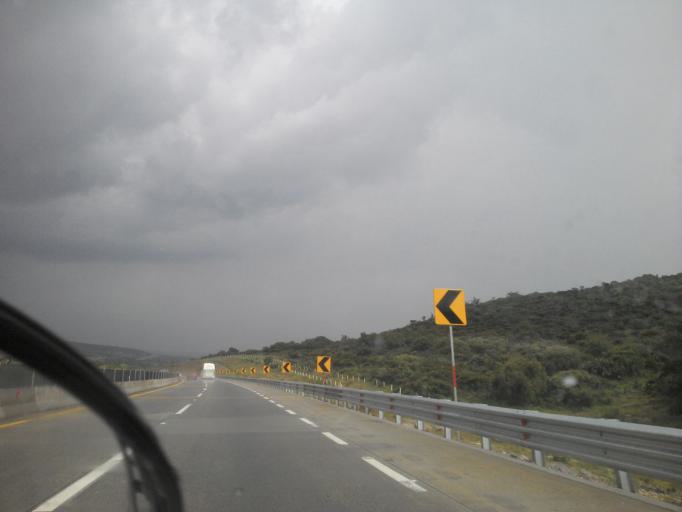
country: MX
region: Morelos
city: San Francisco Zacacalco
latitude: 19.9519
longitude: -98.9917
